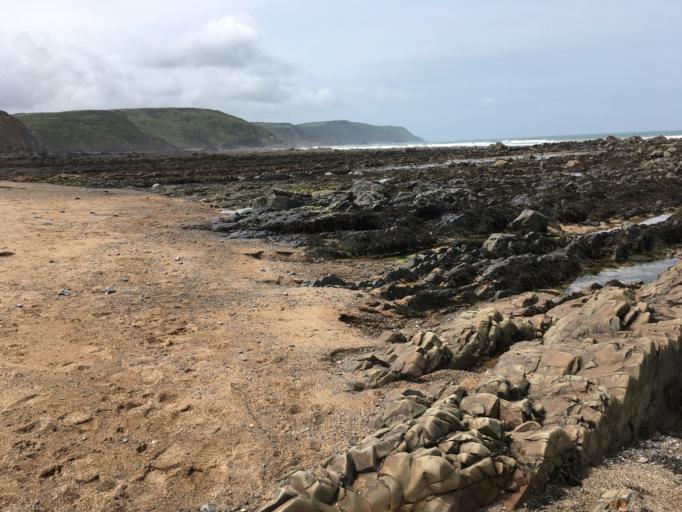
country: GB
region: England
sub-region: Cornwall
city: Poundstock
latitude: 50.7869
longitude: -4.5595
